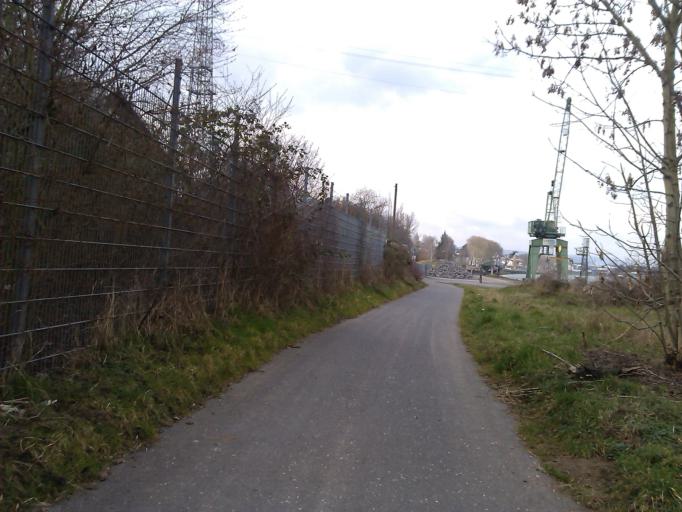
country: DE
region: Rheinland-Pfalz
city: Kettig
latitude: 50.4112
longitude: 7.4737
